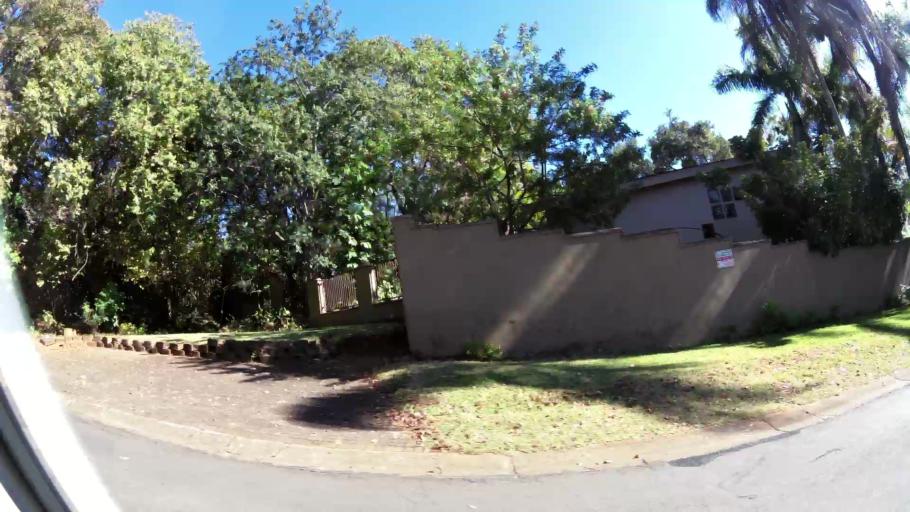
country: ZA
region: Limpopo
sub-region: Mopani District Municipality
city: Tzaneen
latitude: -23.8262
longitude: 30.1466
